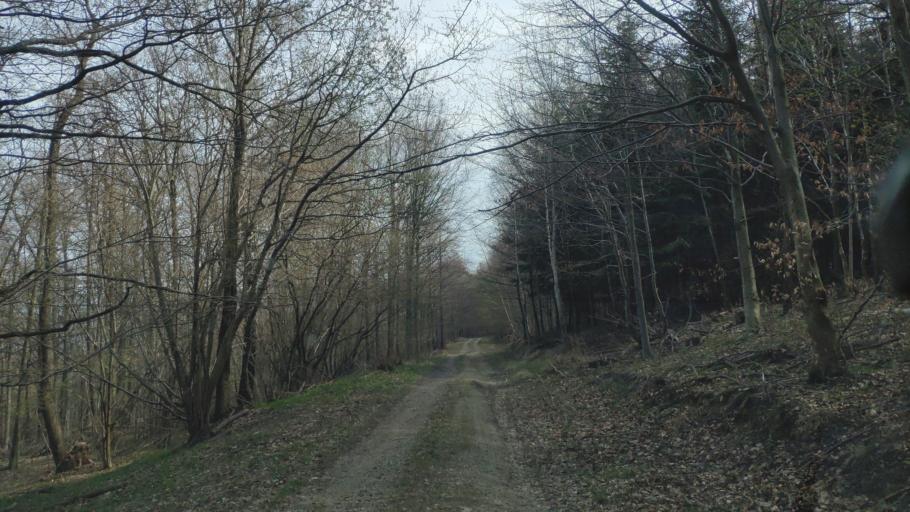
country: SK
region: Kosicky
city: Moldava nad Bodvou
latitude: 48.7376
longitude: 21.0560
